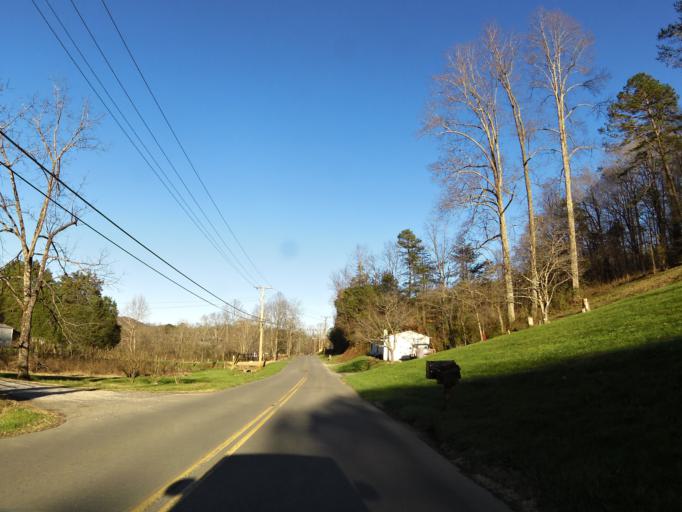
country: US
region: Tennessee
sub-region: Anderson County
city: Oak Ridge
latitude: 36.0848
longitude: -84.2432
